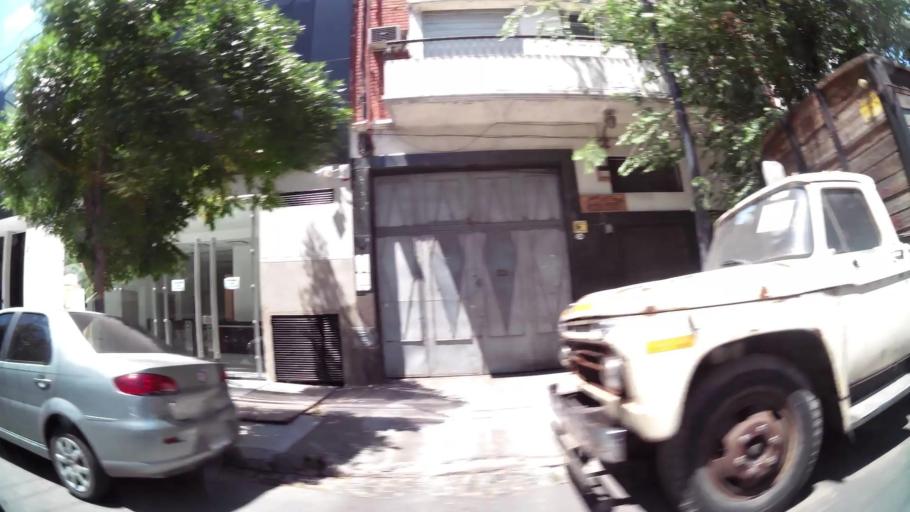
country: AR
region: Buenos Aires F.D.
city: Buenos Aires
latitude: -34.6374
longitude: -58.4008
